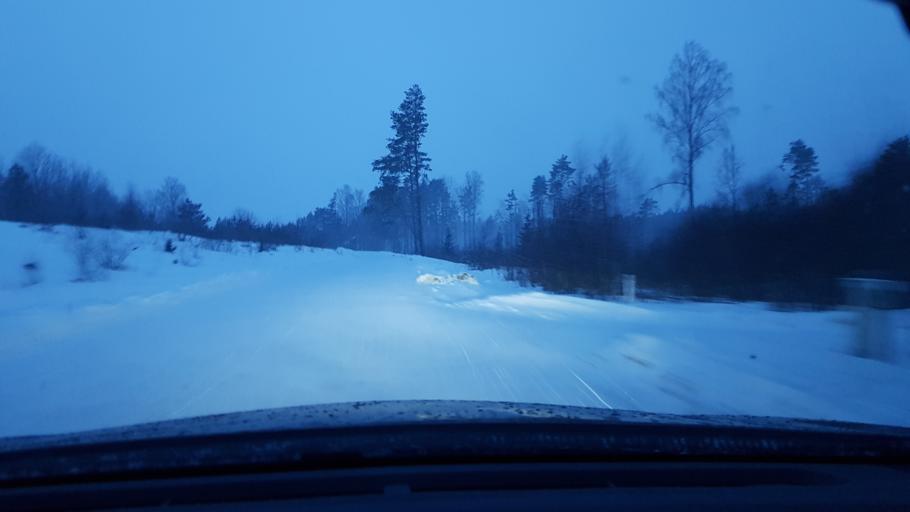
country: EE
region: Harju
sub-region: Kuusalu vald
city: Kuusalu
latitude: 59.4498
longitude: 25.5712
